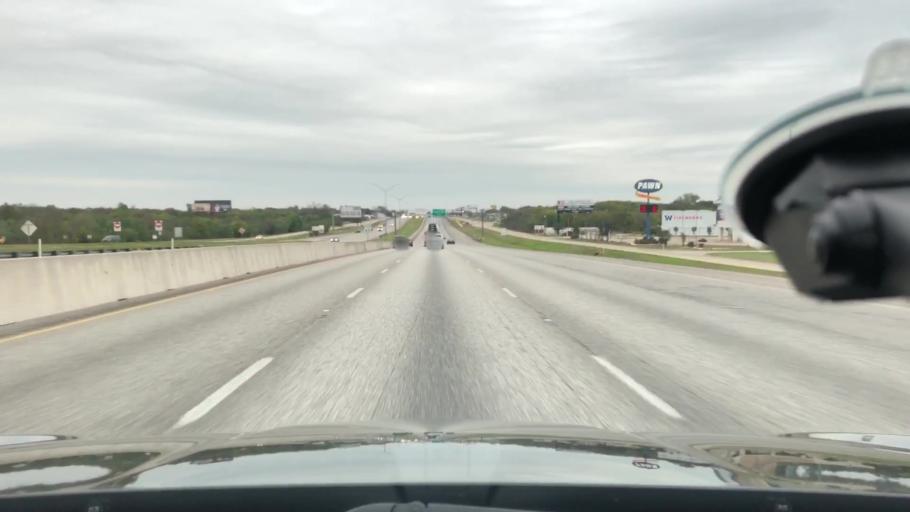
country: US
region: Texas
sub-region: McLennan County
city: Bellmead
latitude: 31.6085
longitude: -97.1043
